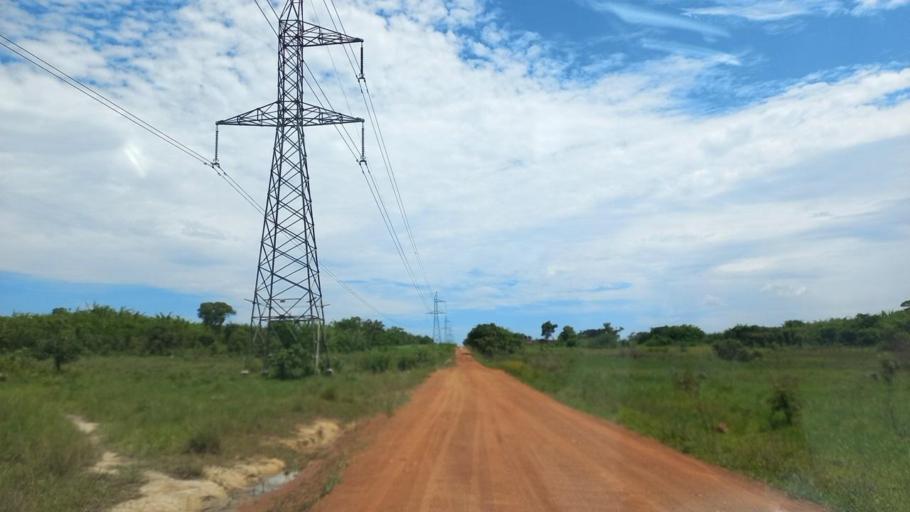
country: ZM
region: Copperbelt
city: Kitwe
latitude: -12.8090
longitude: 28.3607
